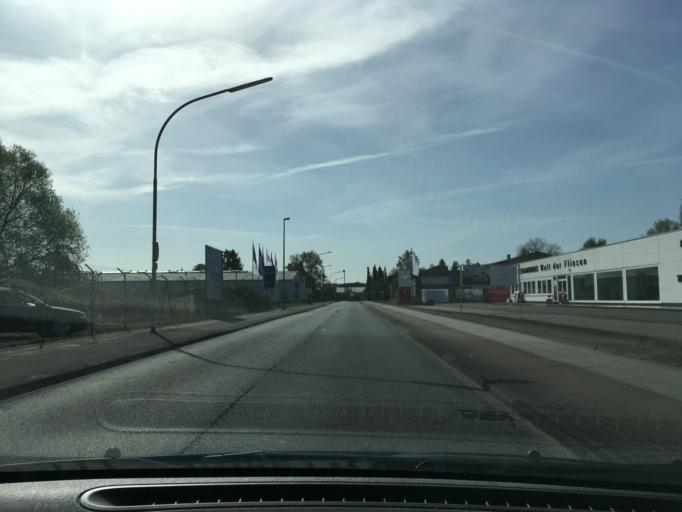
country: DE
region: Lower Saxony
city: Lueneburg
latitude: 53.2711
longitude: 10.4156
